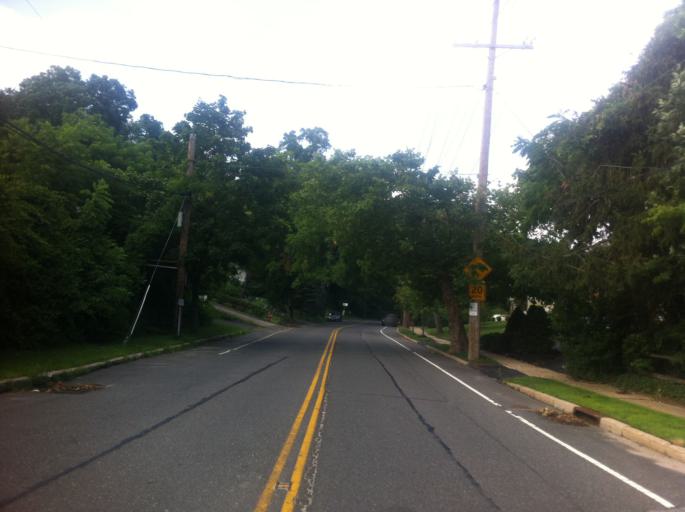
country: US
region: New York
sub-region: Nassau County
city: Glenwood Landing
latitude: 40.8344
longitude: -73.6494
